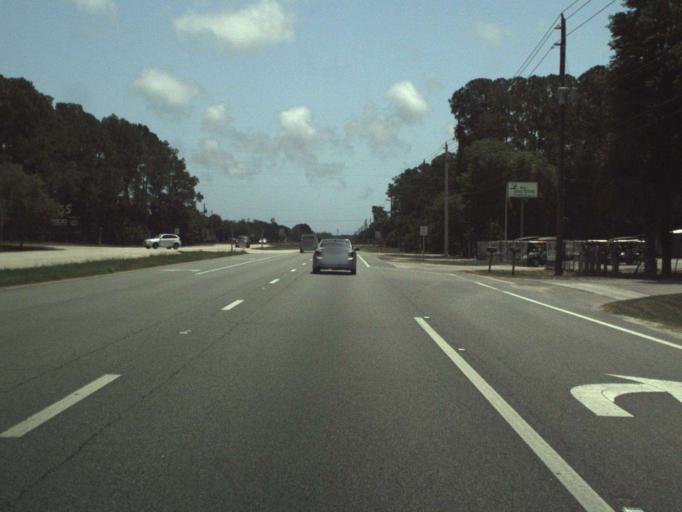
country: US
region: Florida
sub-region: Volusia County
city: Ormond-by-the-Sea
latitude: 29.3332
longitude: -81.1277
